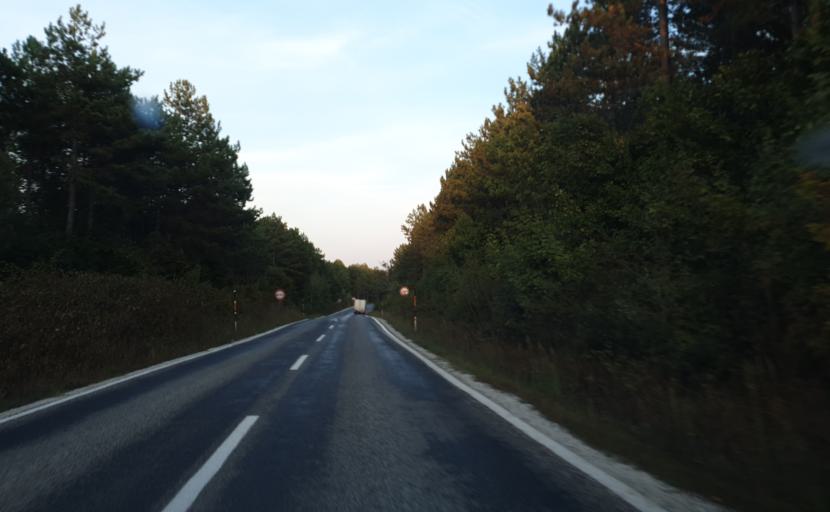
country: TR
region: Kirklareli
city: Igneada
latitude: 41.8622
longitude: 27.8747
